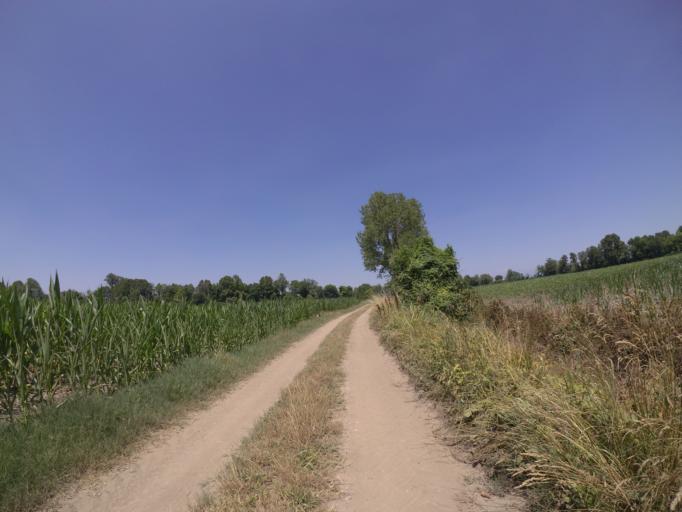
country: IT
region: Friuli Venezia Giulia
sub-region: Provincia di Udine
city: Talmassons
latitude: 45.9206
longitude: 13.0927
